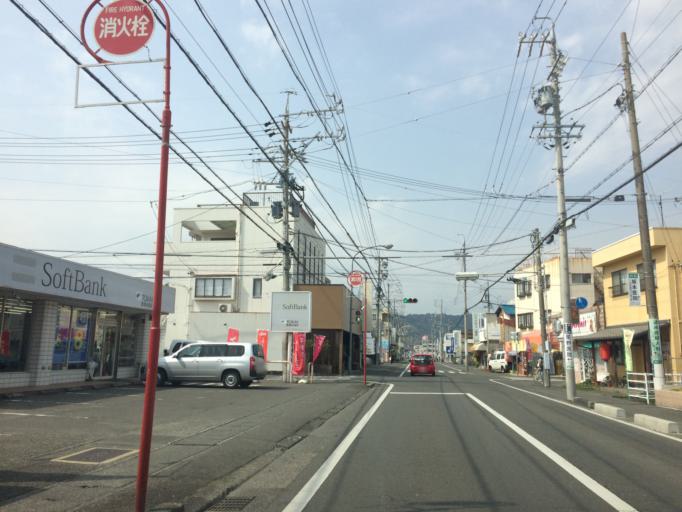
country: JP
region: Shizuoka
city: Shizuoka-shi
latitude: 34.9950
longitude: 138.3968
